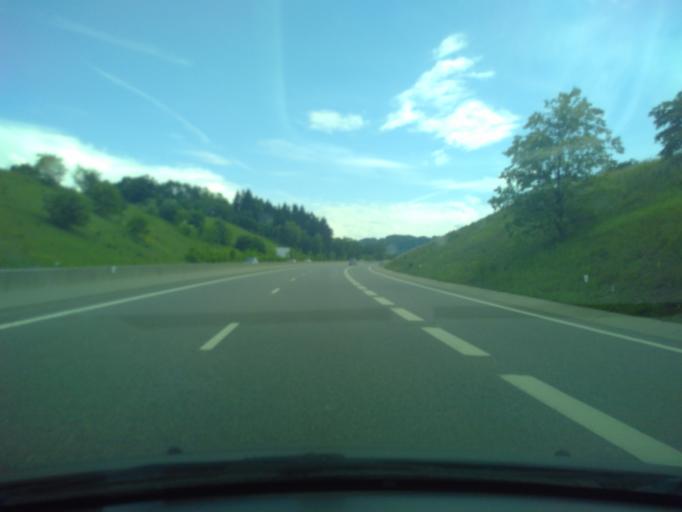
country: FR
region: Rhone-Alpes
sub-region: Departement de la Haute-Savoie
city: Feigeres
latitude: 46.1069
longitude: 6.0946
